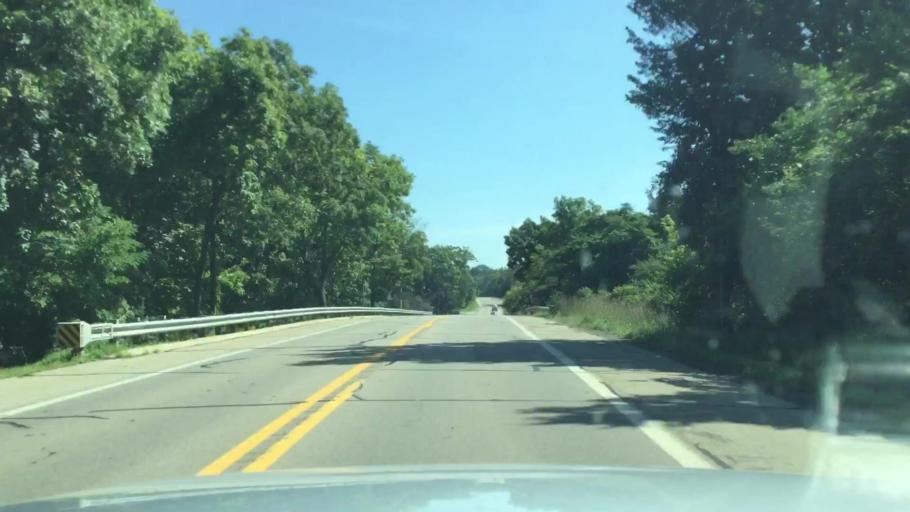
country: US
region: Michigan
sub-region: Jackson County
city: Brooklyn
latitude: 42.0571
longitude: -84.1687
